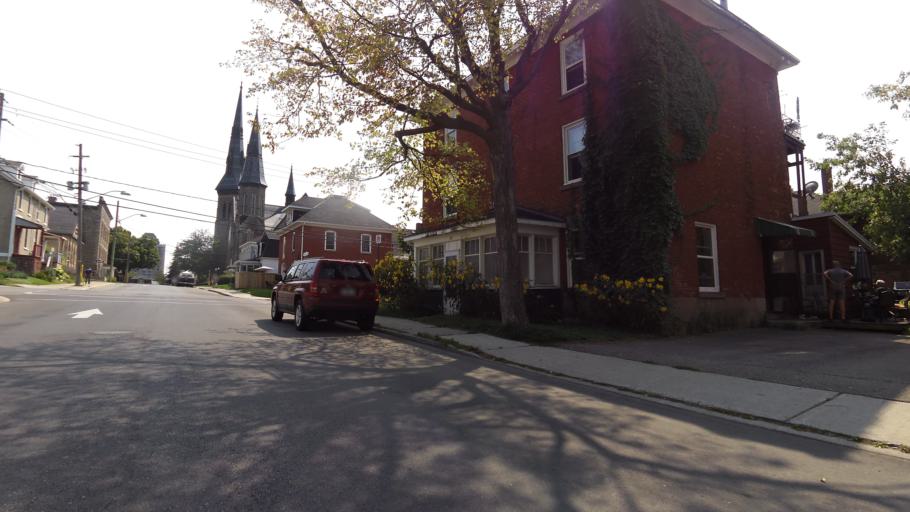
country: CA
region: Ontario
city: Brockville
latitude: 44.5914
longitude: -75.6872
